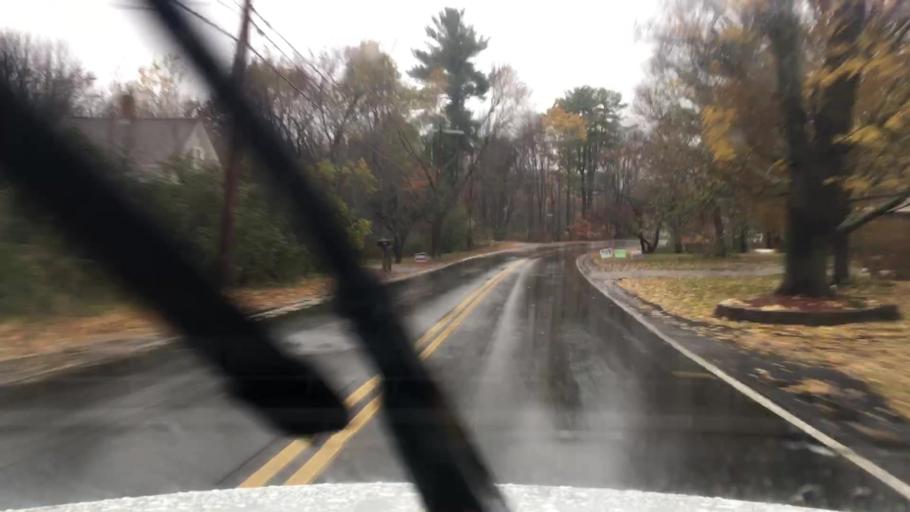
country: US
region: New Hampshire
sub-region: Strafford County
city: Rochester
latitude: 43.3287
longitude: -70.9565
